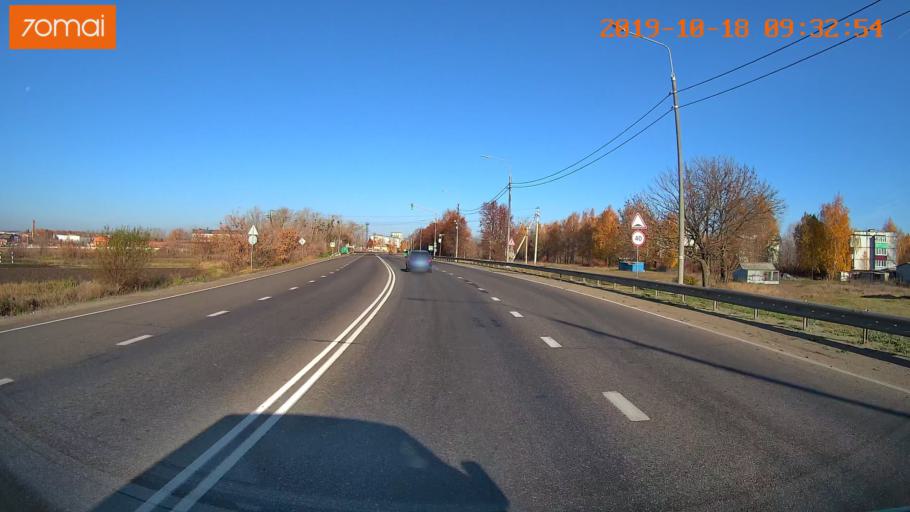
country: RU
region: Tula
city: Yefremov
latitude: 53.1620
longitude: 38.1544
